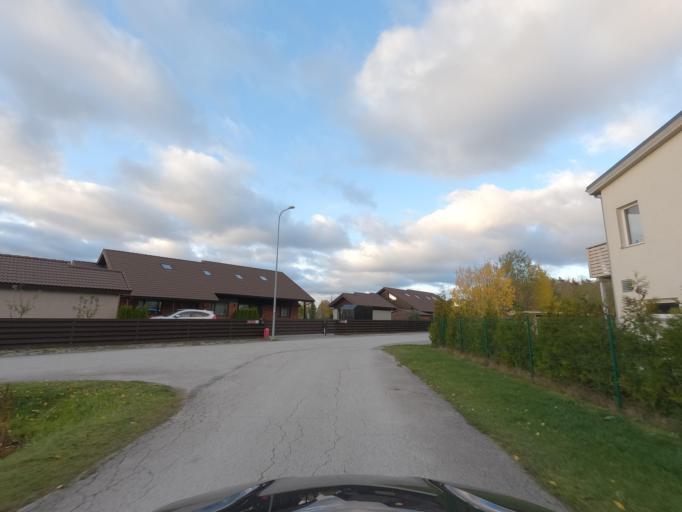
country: EE
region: Harju
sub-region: Kiili vald
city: Kiili
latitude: 59.3656
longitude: 24.8144
